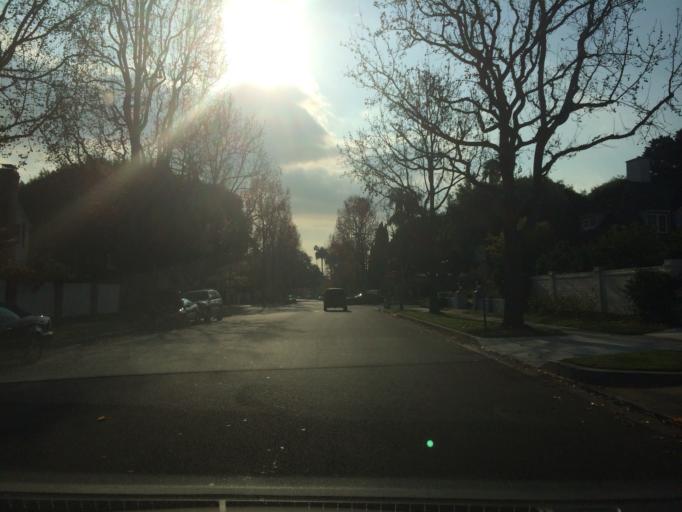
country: US
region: California
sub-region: Los Angeles County
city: Beverly Hills
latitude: 34.0738
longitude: -118.4073
